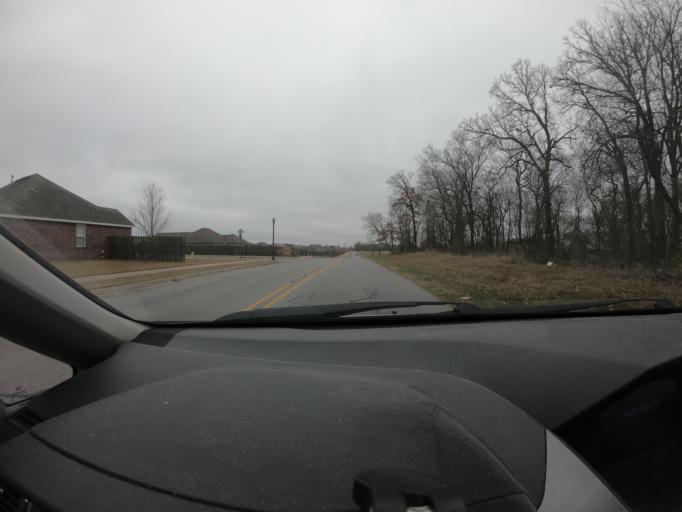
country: US
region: Arkansas
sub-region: Benton County
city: Bentonville
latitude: 36.3507
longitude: -94.2402
